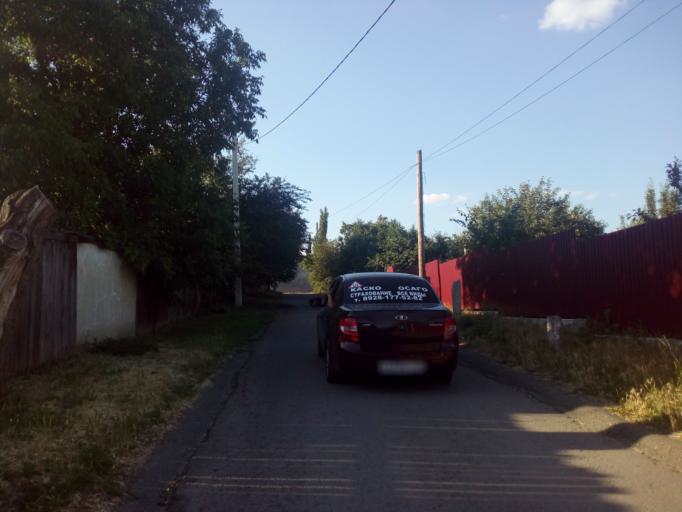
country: RU
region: Rostov
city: Sholokhovskiy
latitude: 48.2771
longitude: 41.0501
